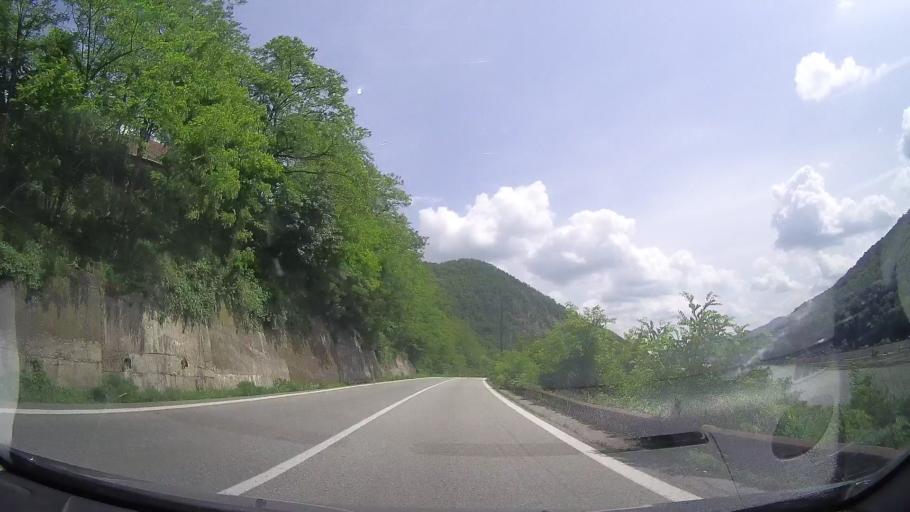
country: RO
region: Valcea
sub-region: Oras Calimanesti
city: Jiblea Veche
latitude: 45.2598
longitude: 24.3336
